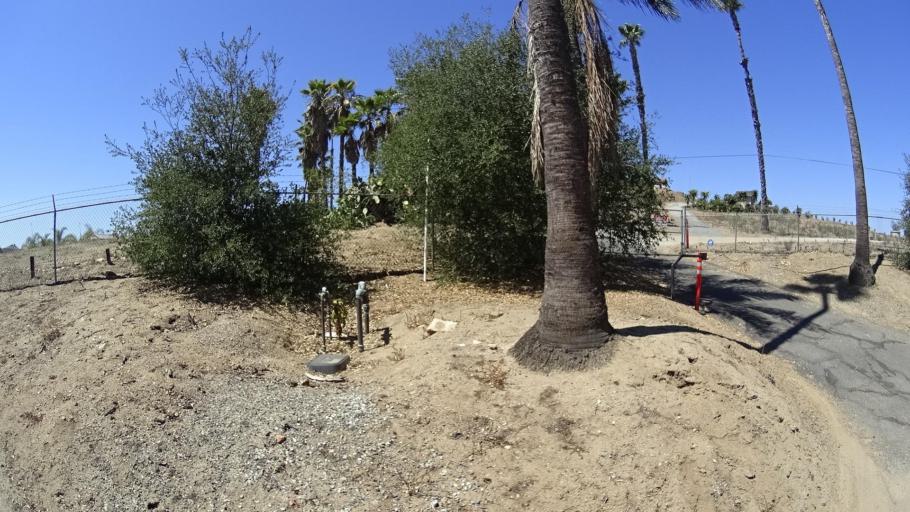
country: US
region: California
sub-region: San Diego County
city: Bonsall
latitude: 33.3342
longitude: -117.1719
